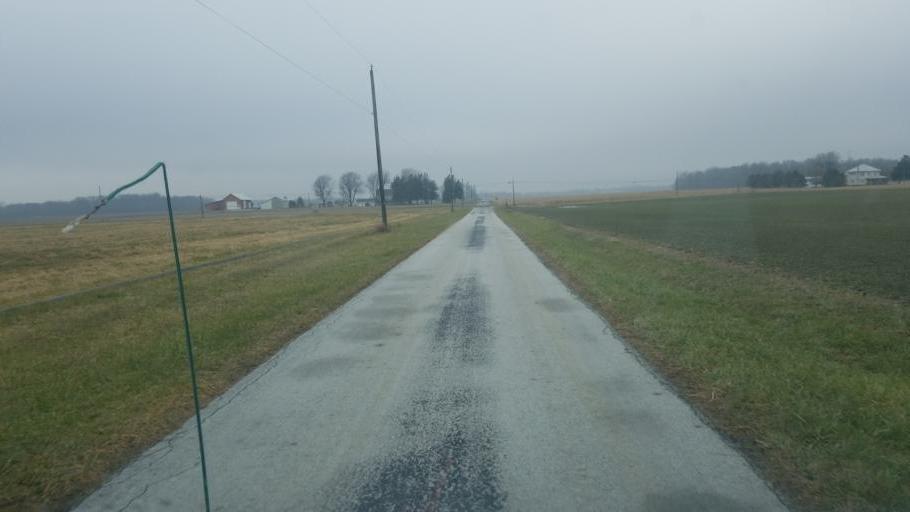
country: US
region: Ohio
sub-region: Hardin County
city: Forest
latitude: 40.6924
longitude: -83.4778
